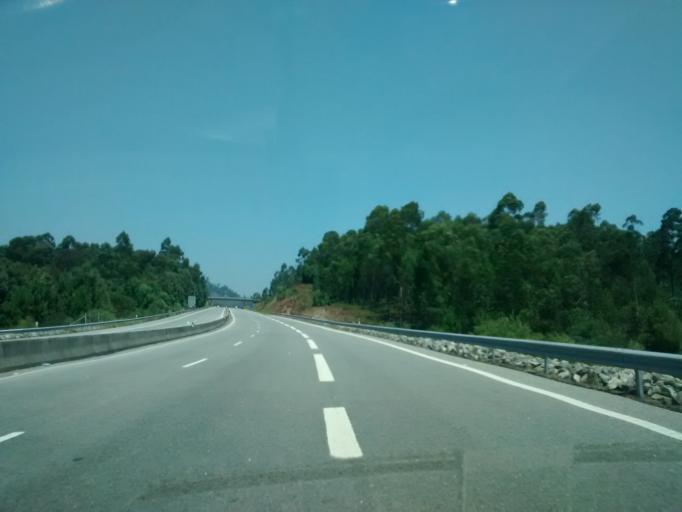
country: PT
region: Viana do Castelo
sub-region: Ponte de Lima
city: Ponte de Lima
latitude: 41.7564
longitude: -8.6758
